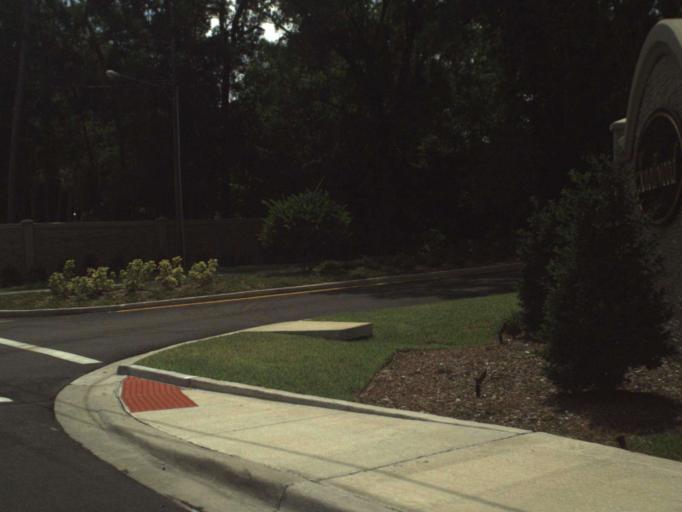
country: US
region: Florida
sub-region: Seminole County
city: Altamonte Springs
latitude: 28.6956
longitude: -81.3799
